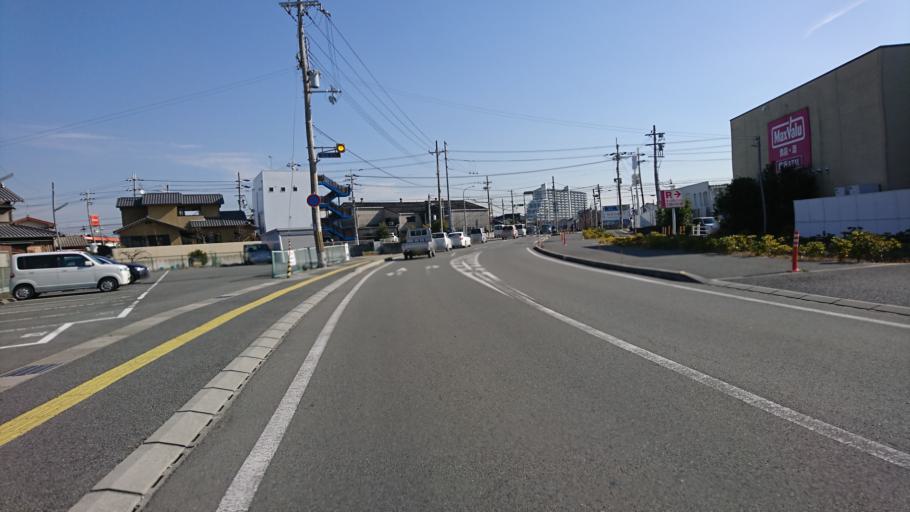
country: JP
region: Hyogo
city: Kakogawacho-honmachi
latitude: 34.7751
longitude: 134.8027
